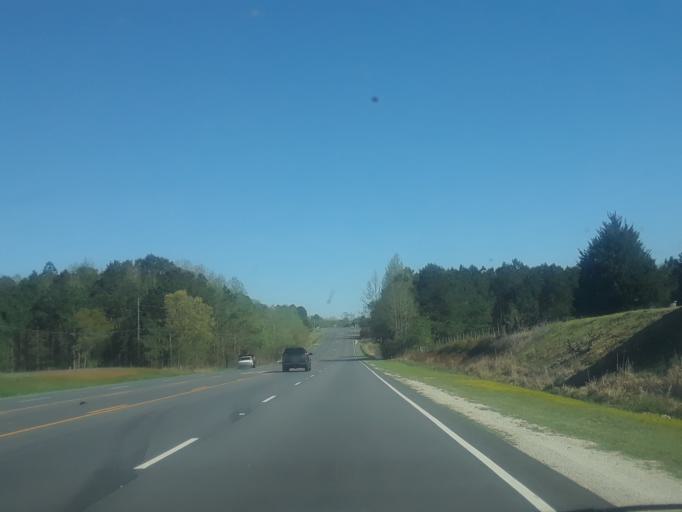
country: US
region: North Carolina
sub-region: Harnett County
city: Buies Creek
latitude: 35.3843
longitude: -78.7214
